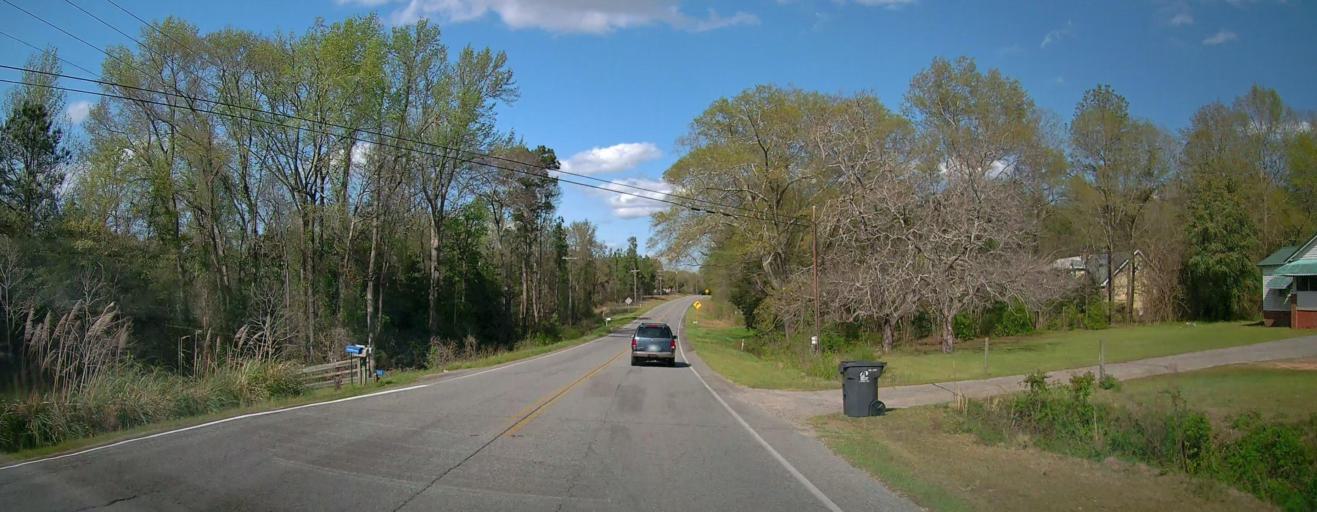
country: US
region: Georgia
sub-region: Baldwin County
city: Hardwick
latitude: 33.0021
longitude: -83.2554
